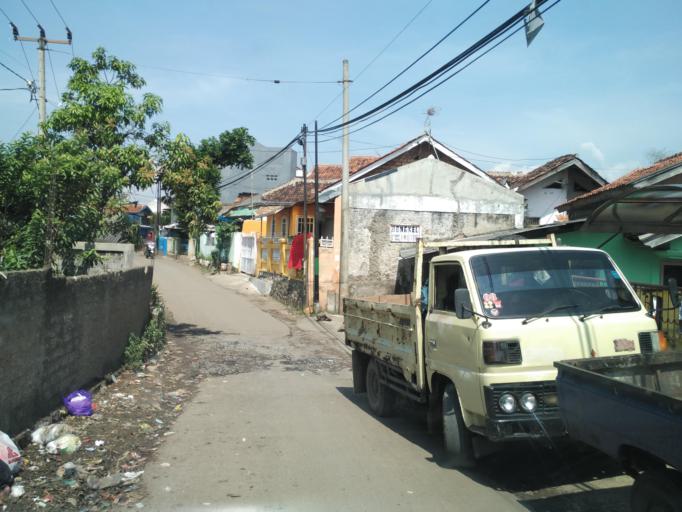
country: ID
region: West Java
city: Ciranjang-hilir
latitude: -6.8210
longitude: 107.1175
